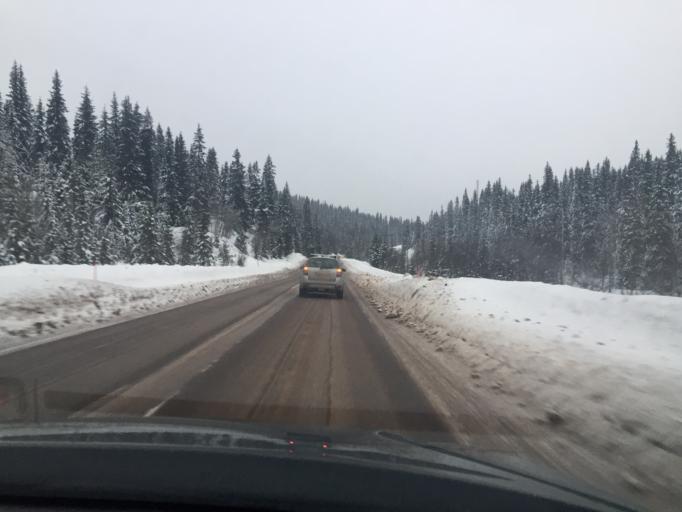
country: SE
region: Dalarna
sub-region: Malung-Saelens kommun
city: Malung
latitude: 61.1623
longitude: 13.1442
